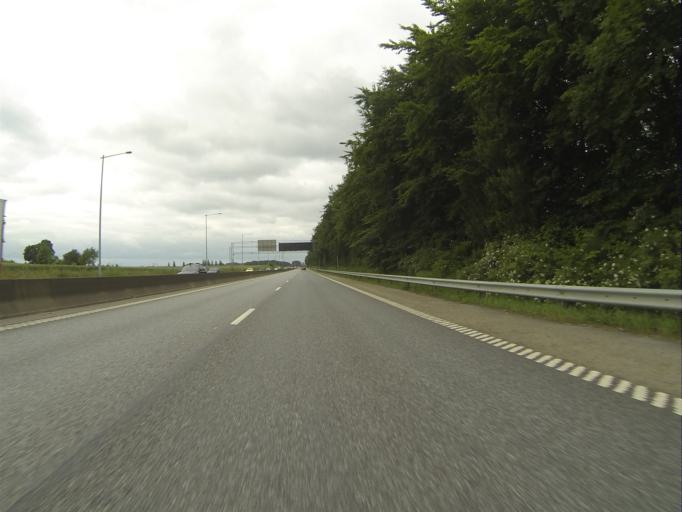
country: SE
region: Skane
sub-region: Burlovs Kommun
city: Arloev
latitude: 55.6326
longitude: 13.0877
